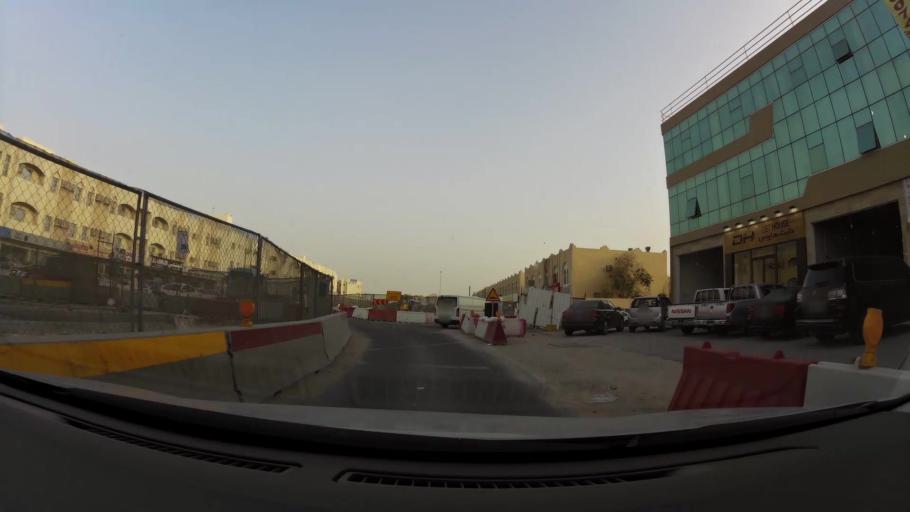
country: QA
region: Baladiyat ar Rayyan
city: Ar Rayyan
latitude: 25.2428
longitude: 51.4549
